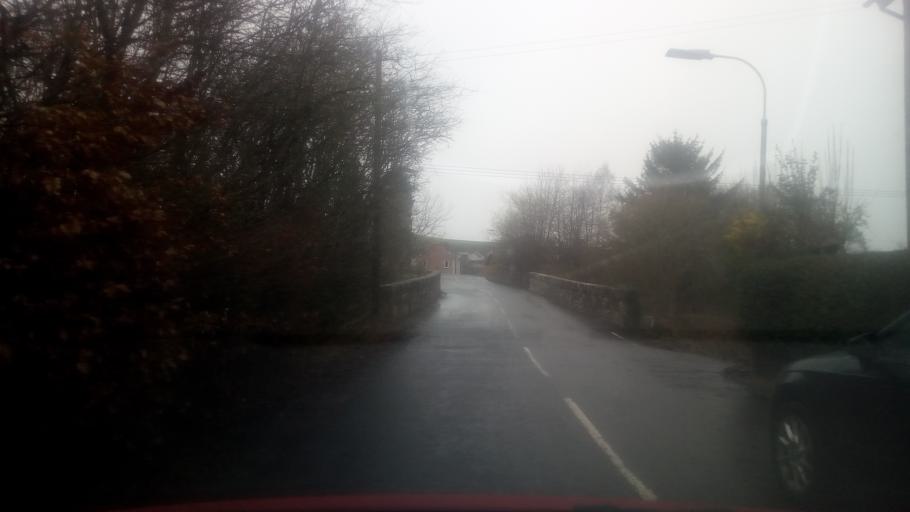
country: GB
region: Scotland
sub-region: The Scottish Borders
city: Earlston
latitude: 55.6358
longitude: -2.6753
